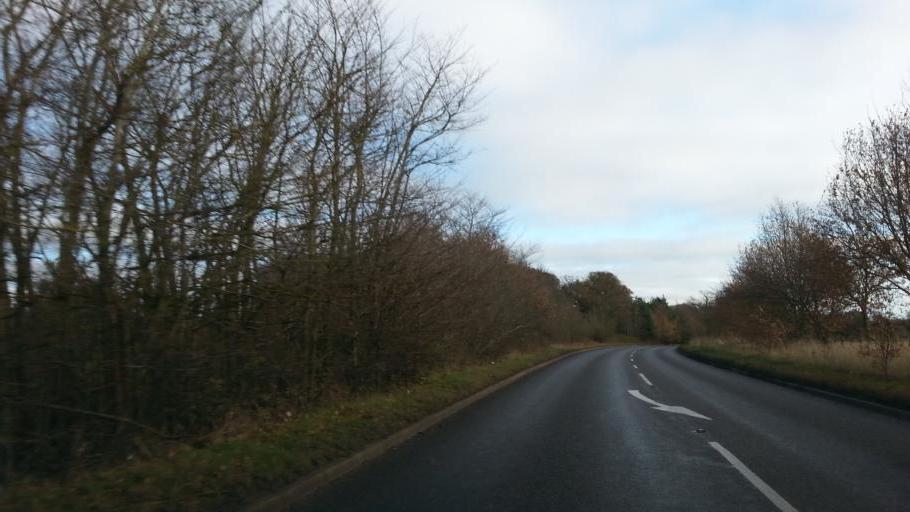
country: GB
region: England
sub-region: Suffolk
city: Wickham Market
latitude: 52.1229
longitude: 1.3967
